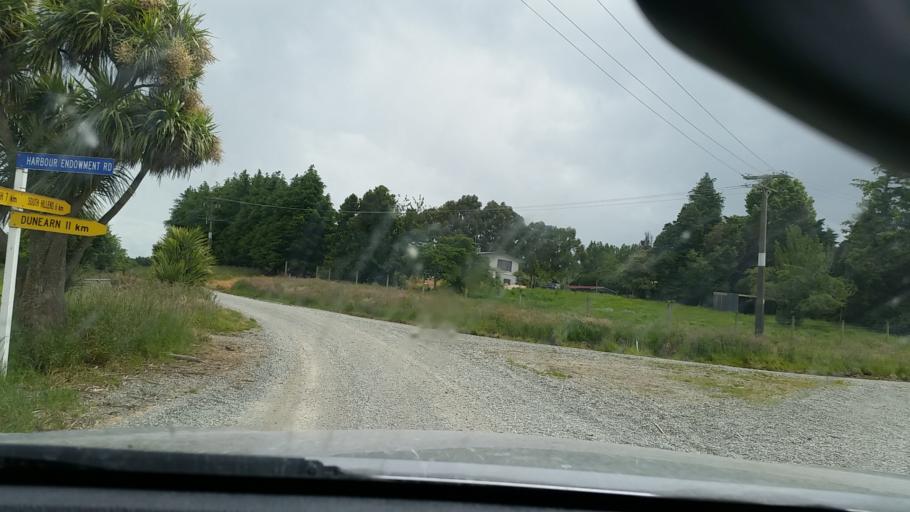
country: NZ
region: Southland
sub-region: Southland District
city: Winton
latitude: -46.0212
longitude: 168.2661
